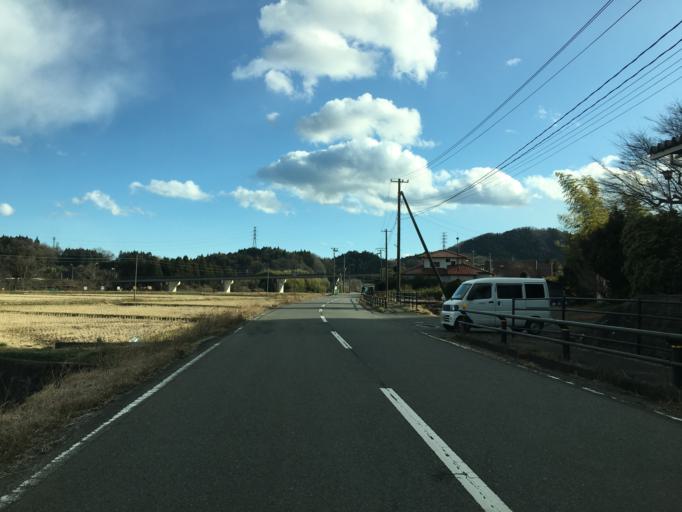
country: JP
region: Ibaraki
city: Kitaibaraki
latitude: 36.9120
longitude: 140.7329
